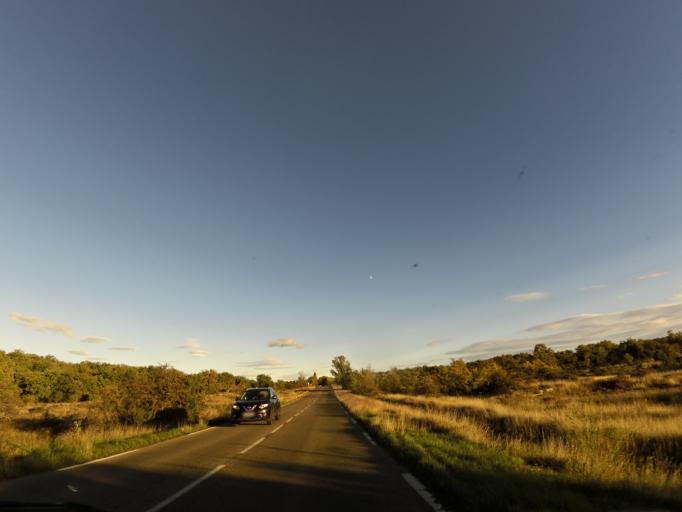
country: FR
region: Languedoc-Roussillon
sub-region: Departement du Gard
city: Saint-Hippolyte-du-Fort
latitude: 43.9501
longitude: 3.8838
